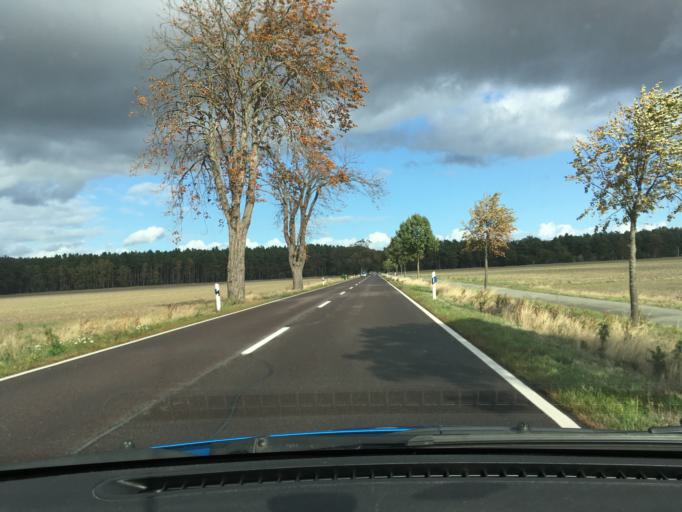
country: DE
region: Saxony-Anhalt
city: Pretzier
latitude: 52.8490
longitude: 11.3502
